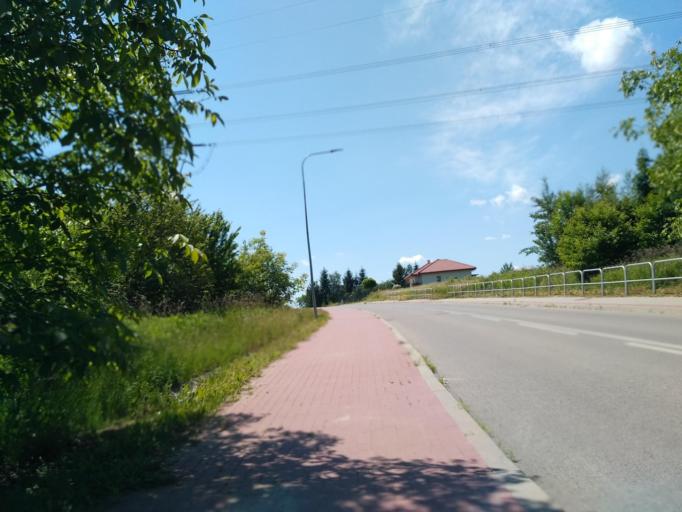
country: PL
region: Subcarpathian Voivodeship
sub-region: Krosno
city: Krosno
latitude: 49.7095
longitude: 21.7820
